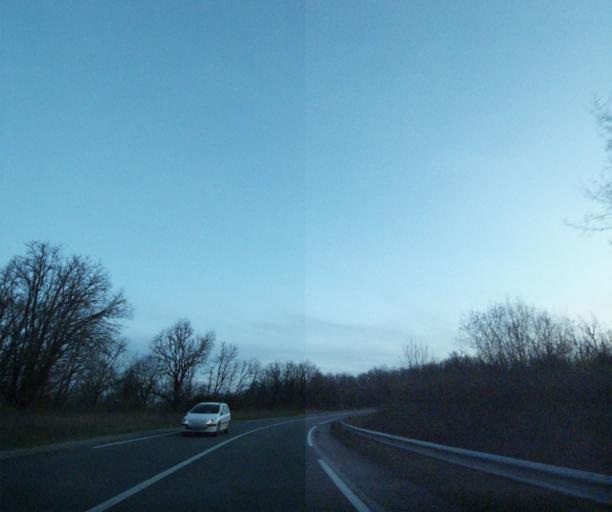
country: FR
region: Midi-Pyrenees
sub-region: Departement du Lot
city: Pradines
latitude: 44.5295
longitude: 1.4666
